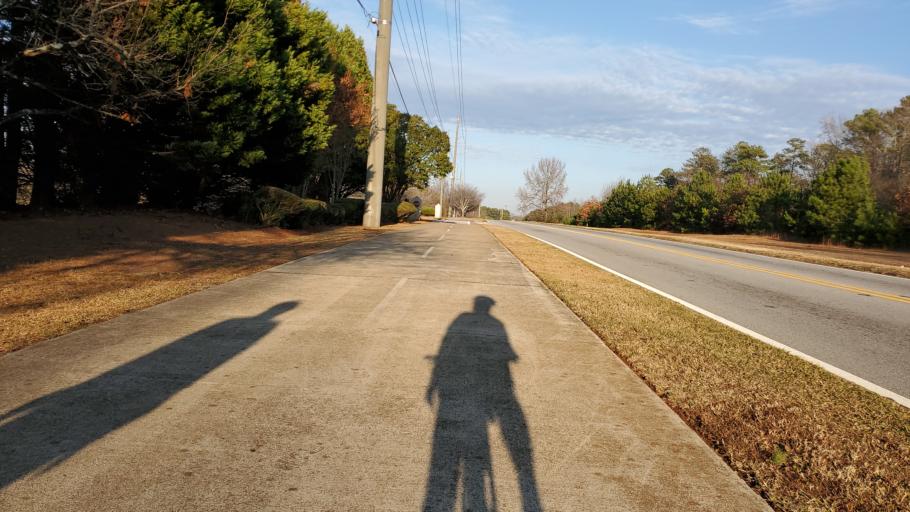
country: US
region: Georgia
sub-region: DeKalb County
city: Clarkston
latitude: 33.8214
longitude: -84.2076
